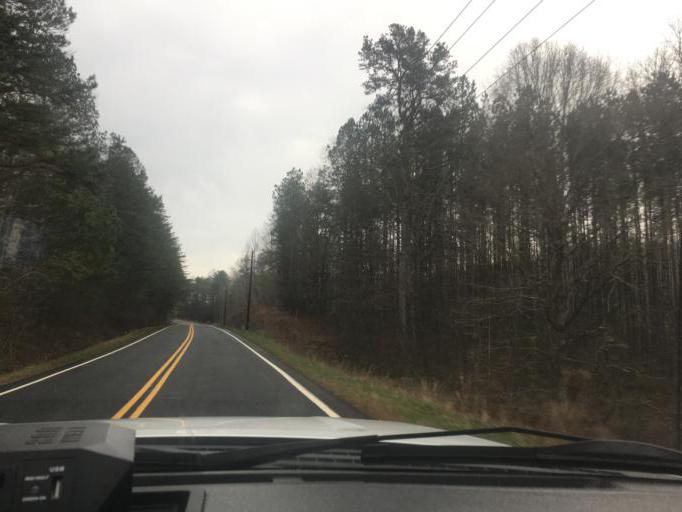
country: US
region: Georgia
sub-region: Dawson County
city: Dawsonville
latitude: 34.3453
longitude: -84.2057
